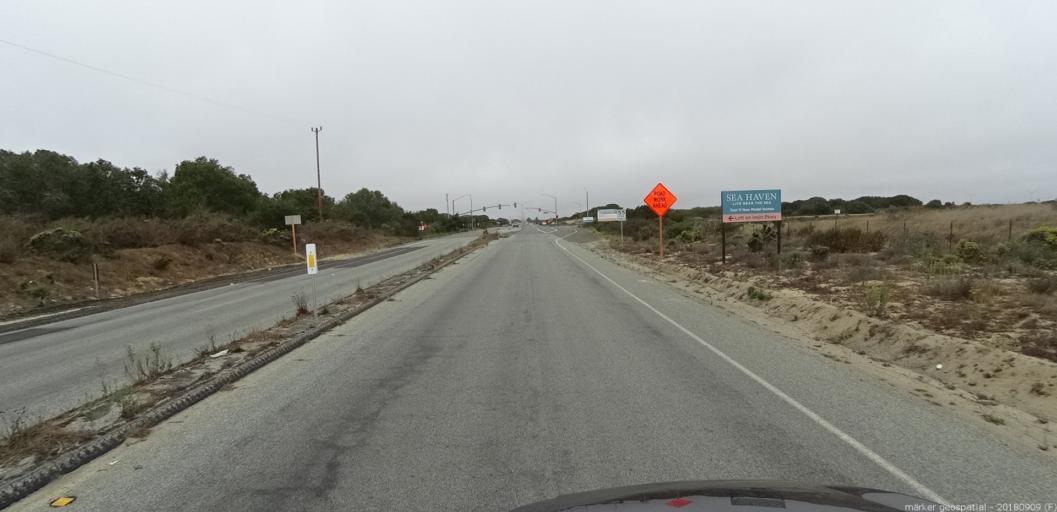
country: US
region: California
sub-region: Monterey County
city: Marina
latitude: 36.6661
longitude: -121.7549
